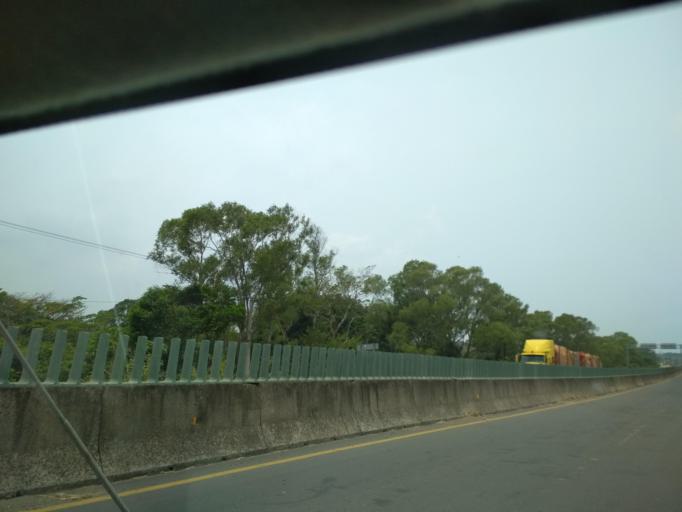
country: MX
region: Veracruz
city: Paso del Toro
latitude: 19.0276
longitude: -96.1406
